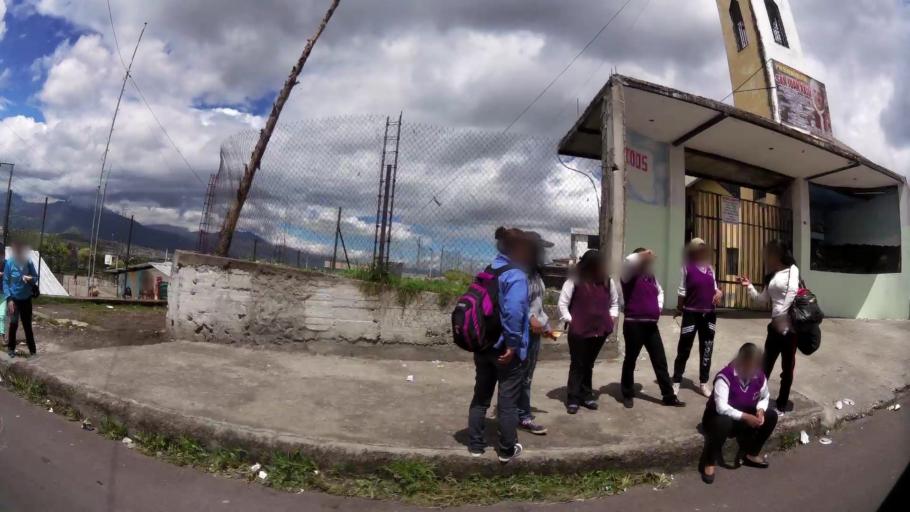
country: EC
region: Pichincha
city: Sangolqui
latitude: -0.3432
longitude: -78.5640
